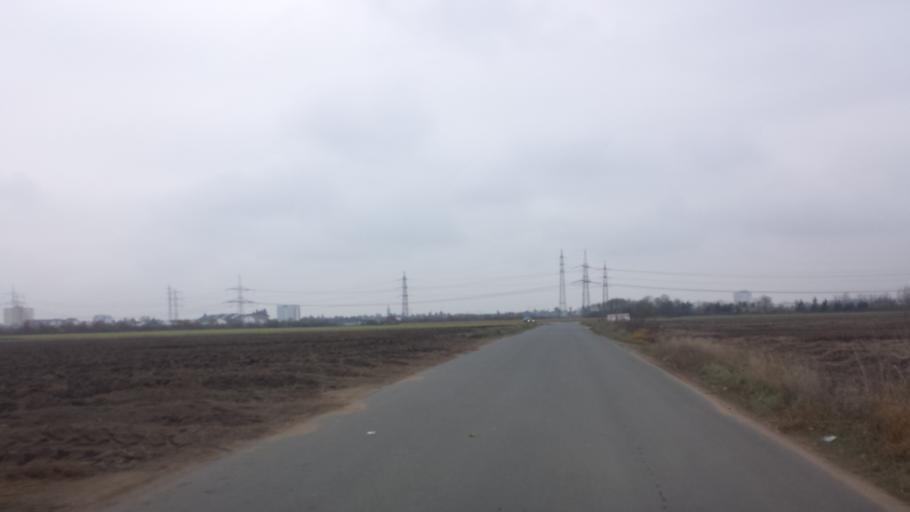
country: DE
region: Hesse
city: Lampertheim
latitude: 49.6160
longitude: 8.4763
